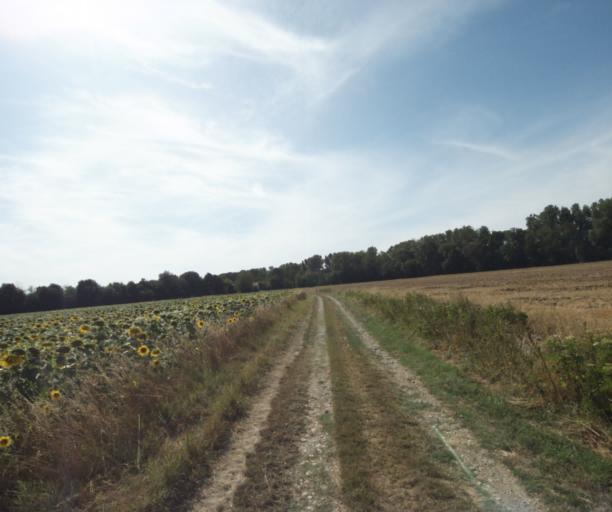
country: FR
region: Midi-Pyrenees
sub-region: Departement du Tarn
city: Soual
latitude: 43.5244
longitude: 2.0730
